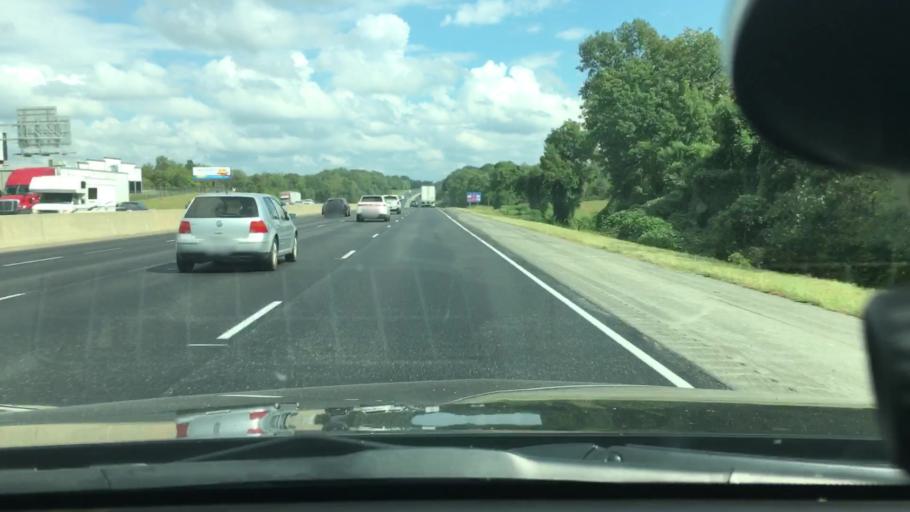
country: US
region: North Carolina
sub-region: Guilford County
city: Gibsonville
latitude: 36.0621
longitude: -79.5442
